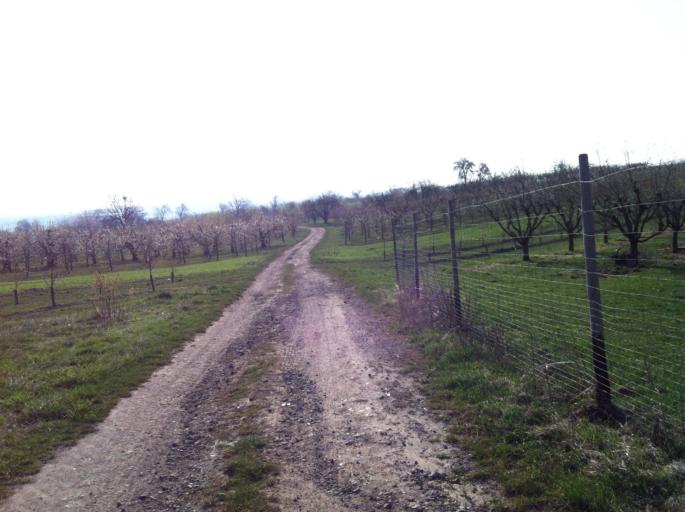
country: DE
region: Rheinland-Pfalz
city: Budenheim
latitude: 49.9846
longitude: 8.1943
